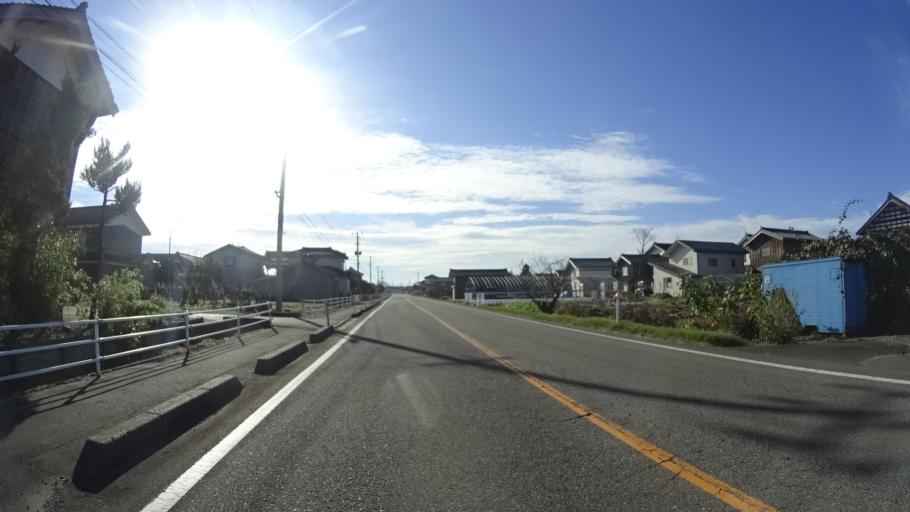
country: JP
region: Niigata
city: Mitsuke
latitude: 37.5800
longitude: 138.8348
